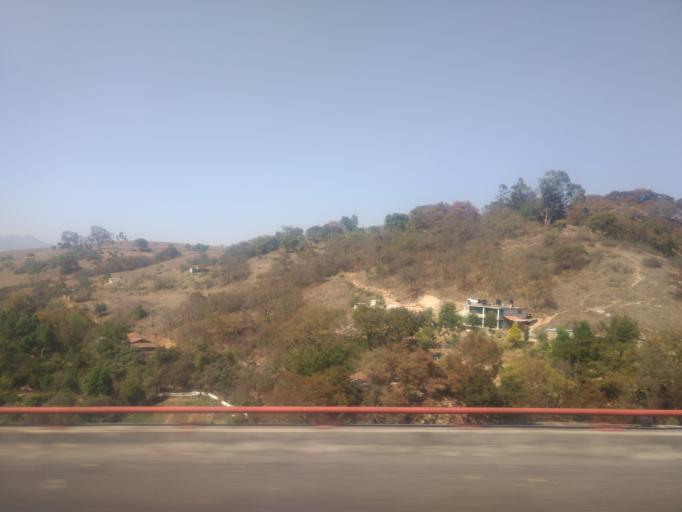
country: MX
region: Hidalgo
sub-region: Acaxochitlan
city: Tlacpac
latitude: 20.1411
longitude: -98.2627
